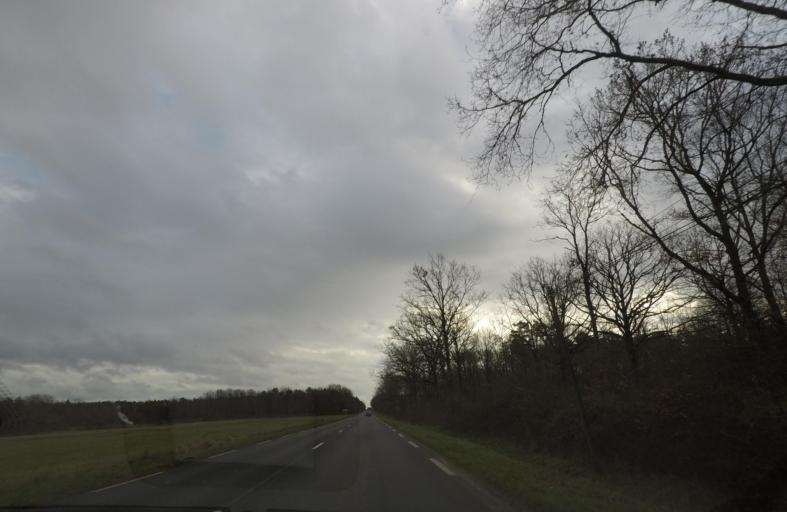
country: FR
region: Centre
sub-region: Departement du Loir-et-Cher
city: Mur-de-Sologne
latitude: 47.4225
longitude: 1.5842
